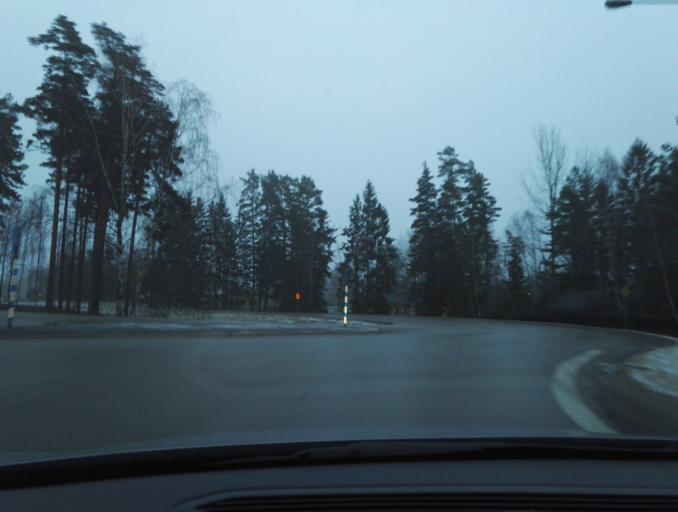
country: SE
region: Kronoberg
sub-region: Vaxjo Kommun
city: Vaexjoe
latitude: 56.8952
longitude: 14.7298
